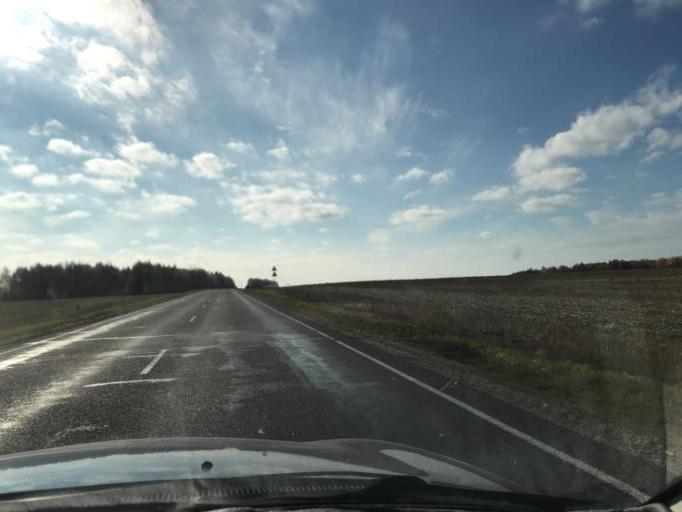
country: BY
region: Grodnenskaya
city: Voranava
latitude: 54.1937
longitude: 25.3452
